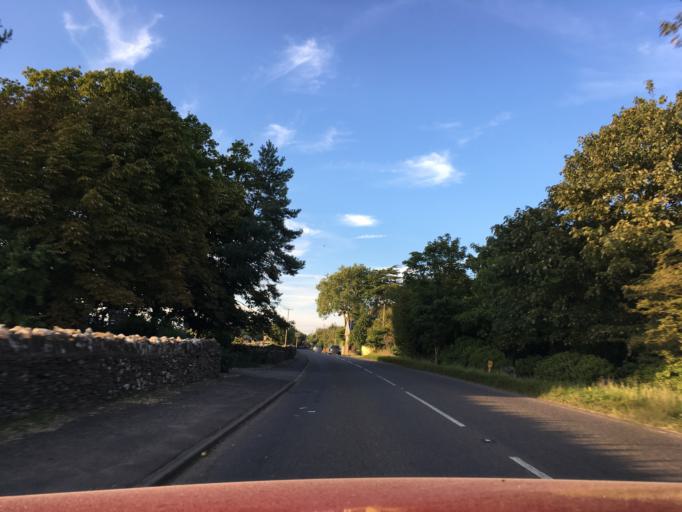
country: GB
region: England
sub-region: South Gloucestershire
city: Yate
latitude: 51.5623
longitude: -2.4504
